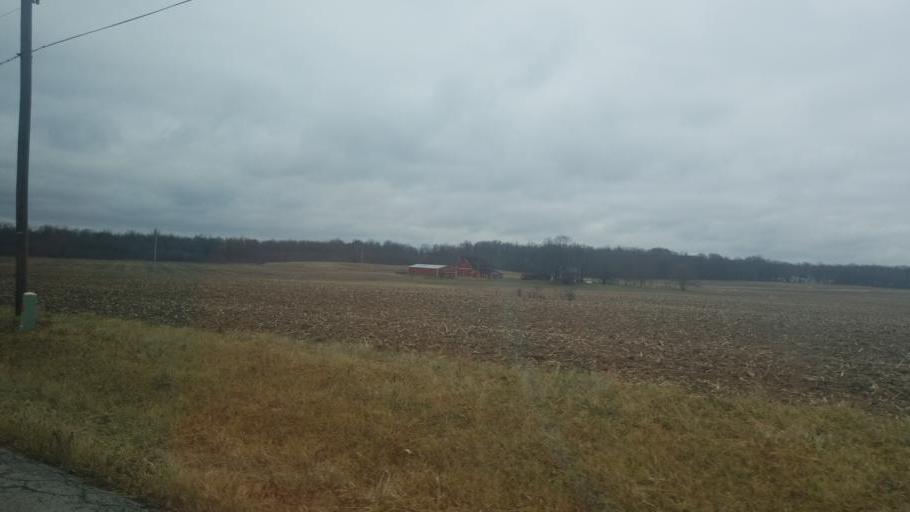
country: US
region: Ohio
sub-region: Crawford County
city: Galion
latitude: 40.7485
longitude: -82.7547
